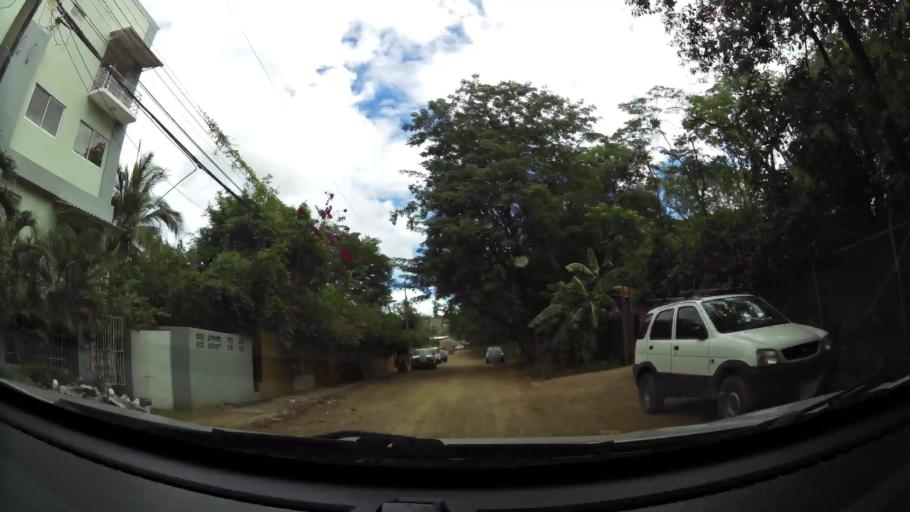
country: CR
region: Guanacaste
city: Santa Cruz
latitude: 10.2946
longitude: -85.8409
